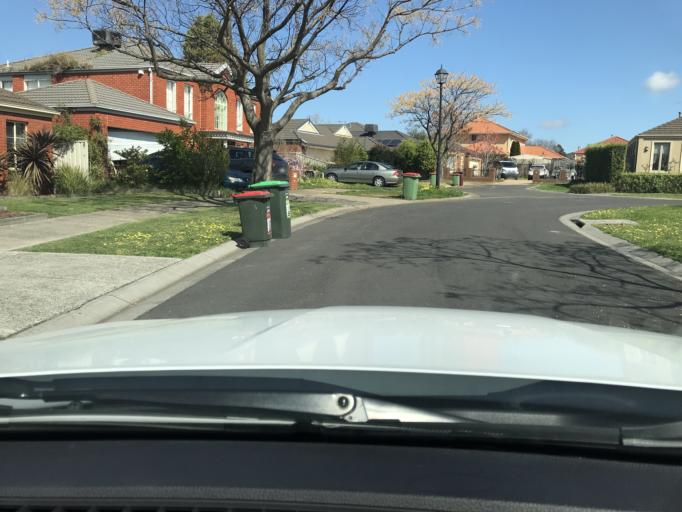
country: AU
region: Victoria
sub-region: Hume
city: Roxburgh Park
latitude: -37.6071
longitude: 144.9186
